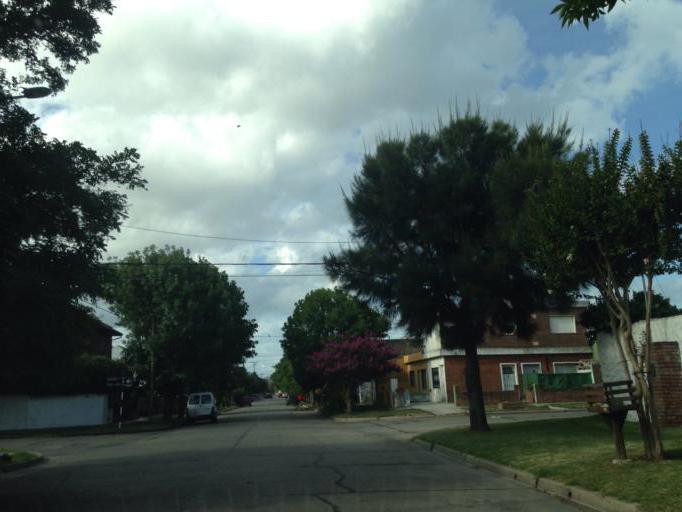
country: AR
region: Buenos Aires
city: Mar del Plata
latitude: -37.9775
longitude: -57.5617
